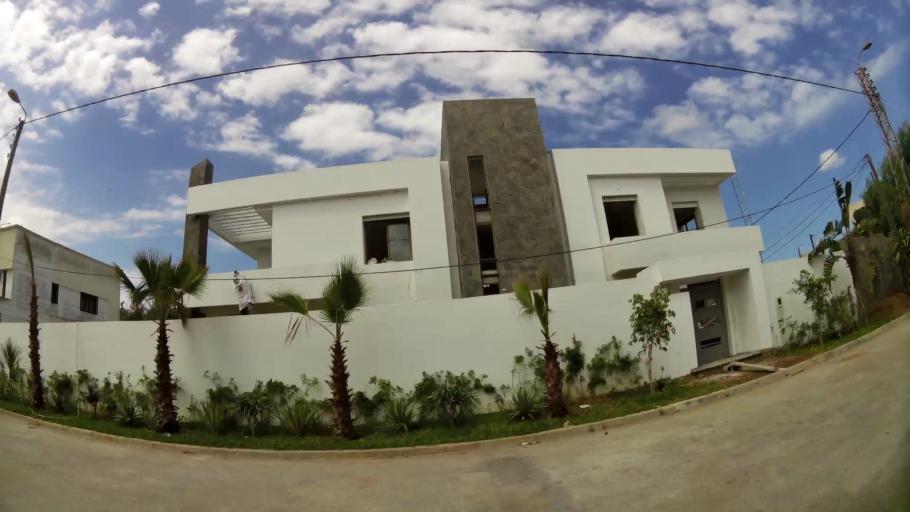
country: MA
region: Gharb-Chrarda-Beni Hssen
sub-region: Kenitra Province
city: Kenitra
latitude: 34.2490
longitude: -6.5966
